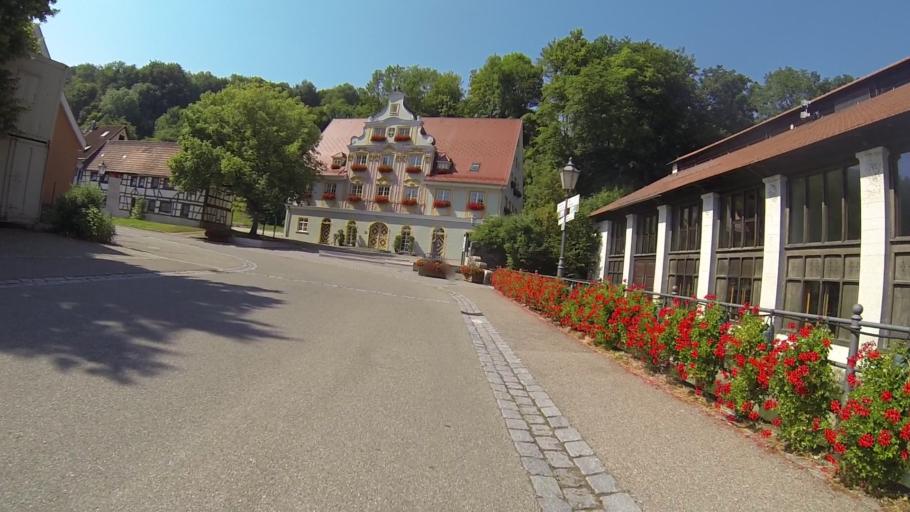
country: DE
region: Baden-Wuerttemberg
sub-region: Regierungsbezirk Stuttgart
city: Konigsbronn
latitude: 48.7378
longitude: 10.1138
